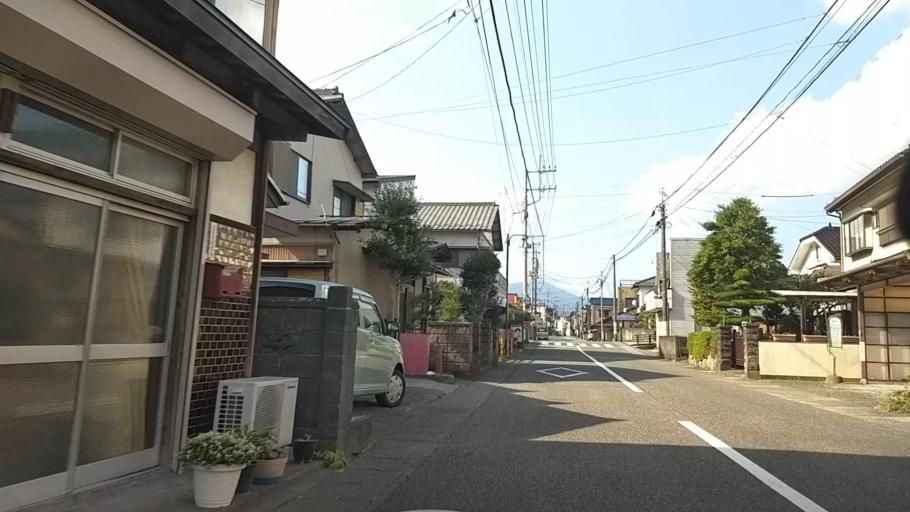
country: JP
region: Shizuoka
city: Fujinomiya
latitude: 35.2852
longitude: 138.4570
